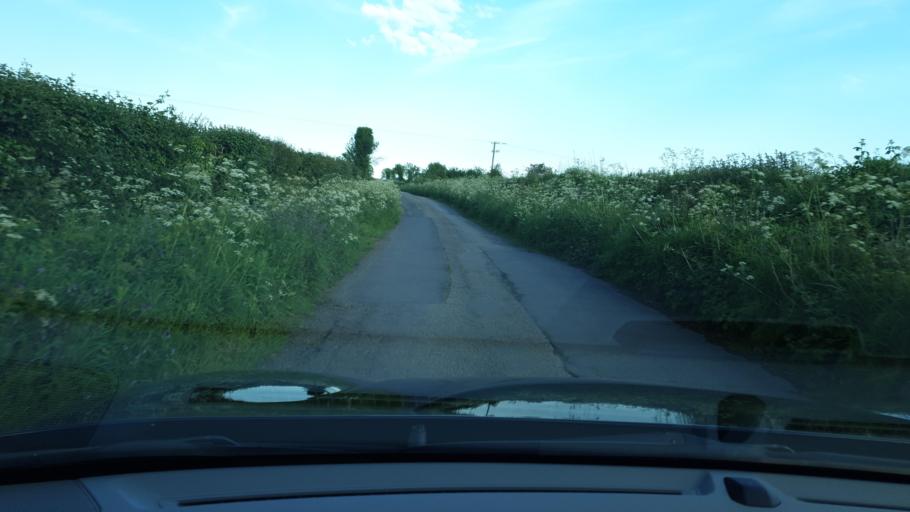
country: IE
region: Leinster
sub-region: An Mhi
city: Ashbourne
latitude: 53.5544
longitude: -6.3634
